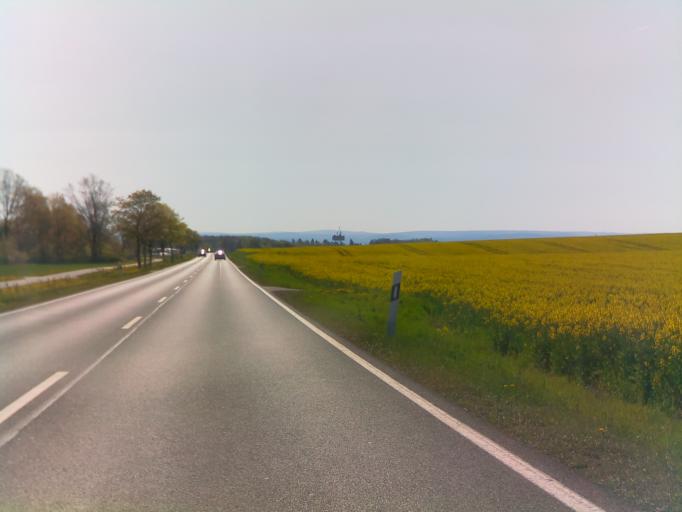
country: DE
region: Saxony
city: Syrau
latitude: 50.5397
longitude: 12.0861
